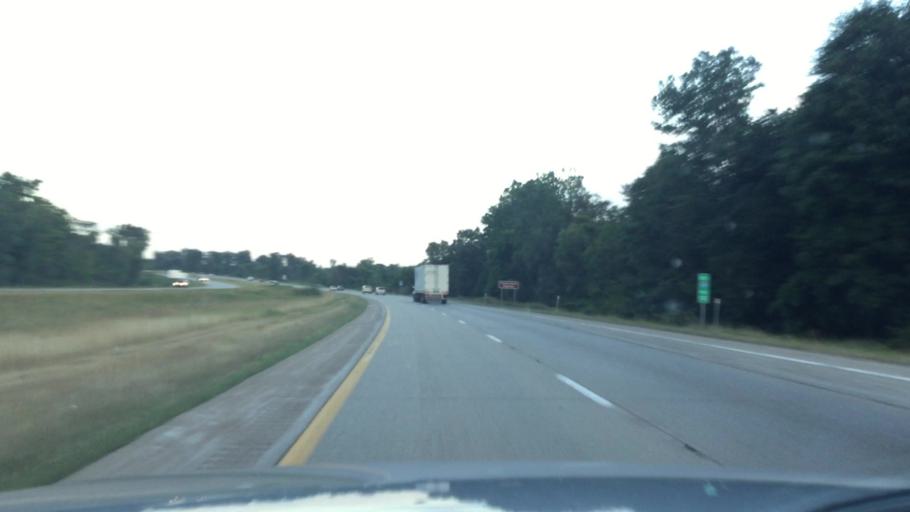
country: US
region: Michigan
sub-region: Shiawassee County
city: Perry
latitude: 42.8393
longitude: -84.2263
